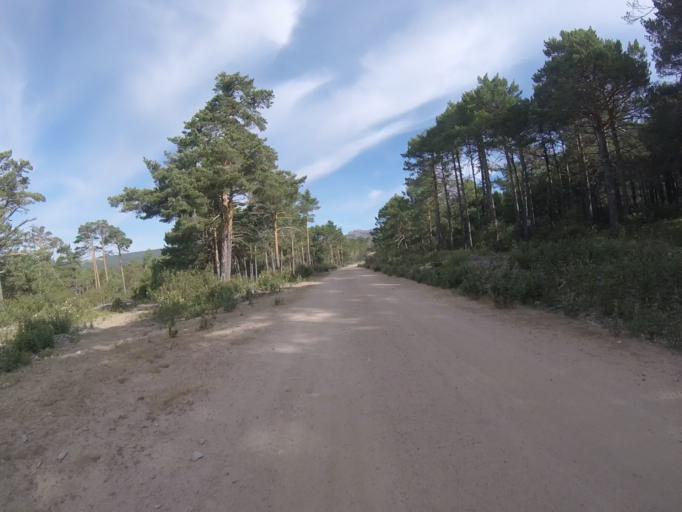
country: ES
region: Castille and Leon
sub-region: Provincia de Avila
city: Peguerinos
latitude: 40.6548
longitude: -4.1843
